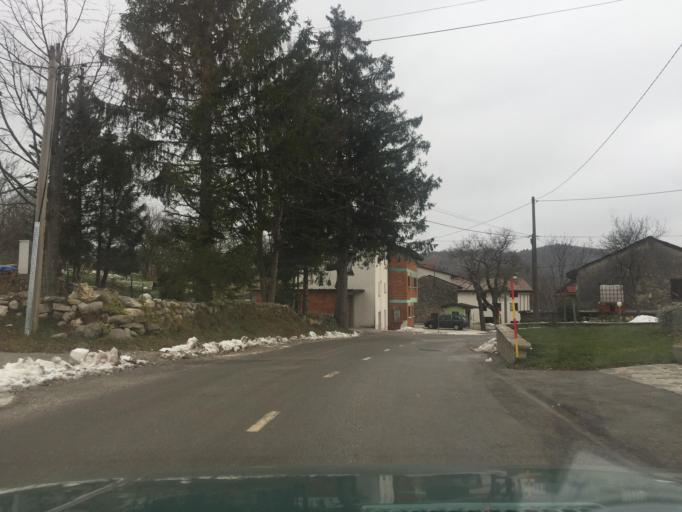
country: SI
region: Kanal
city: Kanal
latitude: 46.0547
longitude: 13.6885
